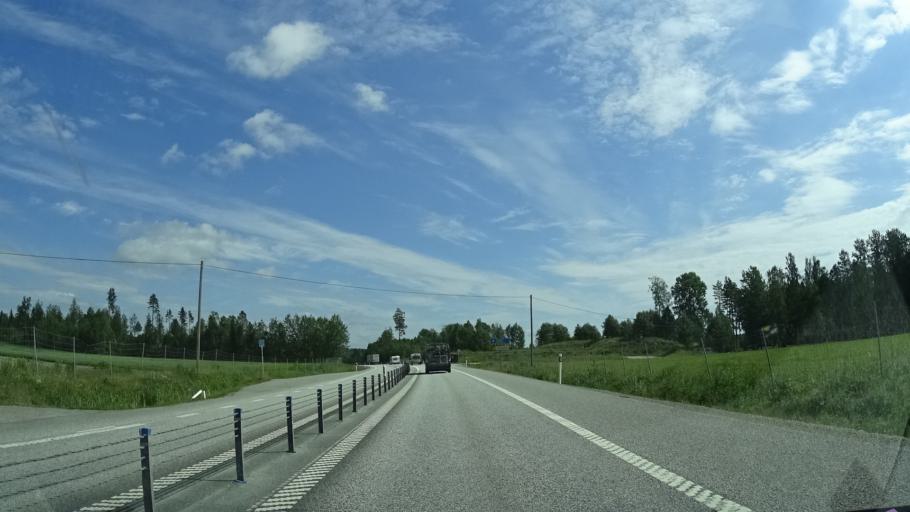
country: SE
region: OErebro
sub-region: Degerfors Kommun
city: Degerfors
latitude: 59.3215
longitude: 14.4099
